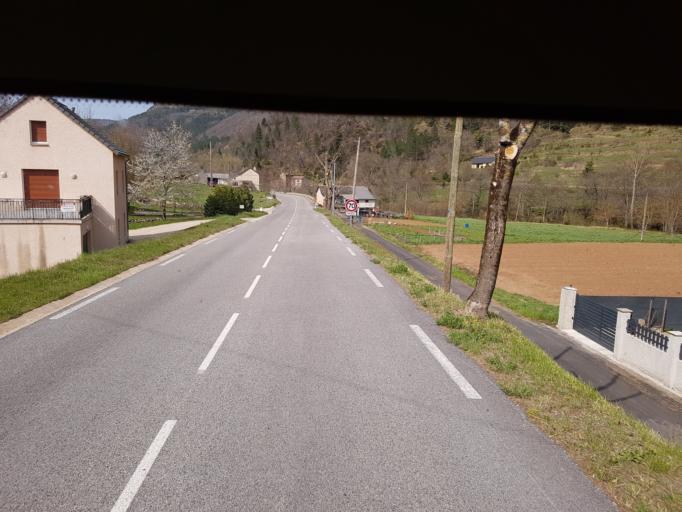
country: FR
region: Languedoc-Roussillon
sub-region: Departement de la Lozere
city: Florac
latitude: 44.3088
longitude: 3.5980
